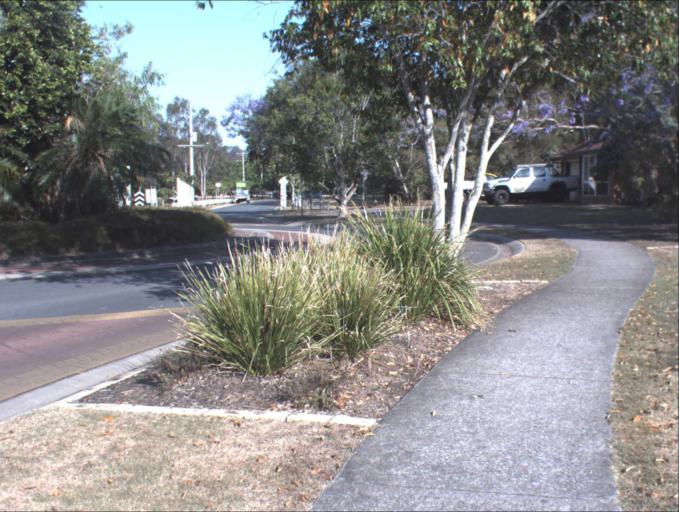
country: AU
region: Queensland
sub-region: Logan
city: Beenleigh
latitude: -27.6998
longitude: 153.1850
